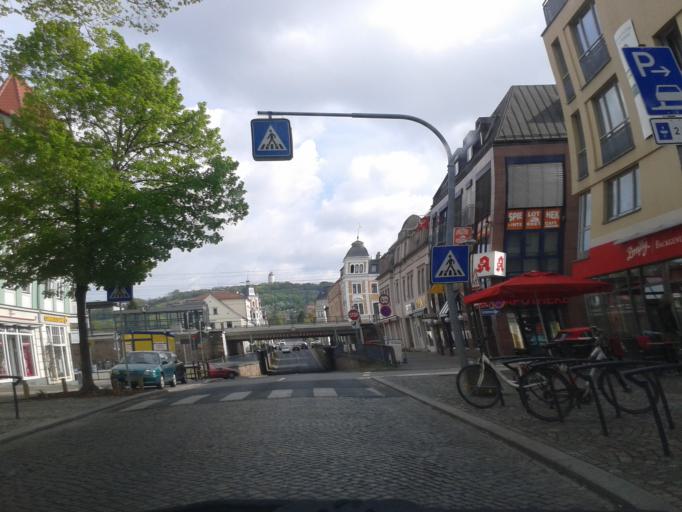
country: DE
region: Saxony
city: Radebeul
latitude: 51.1065
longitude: 13.6293
